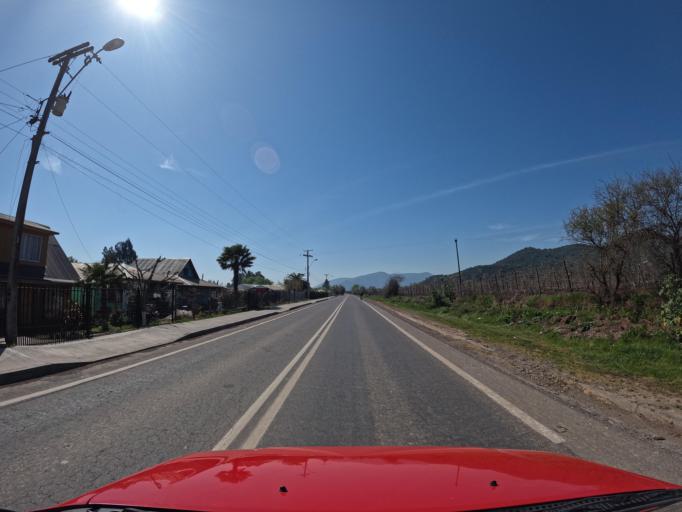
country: CL
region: Maule
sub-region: Provincia de Curico
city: Rauco
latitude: -35.0507
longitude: -71.4731
